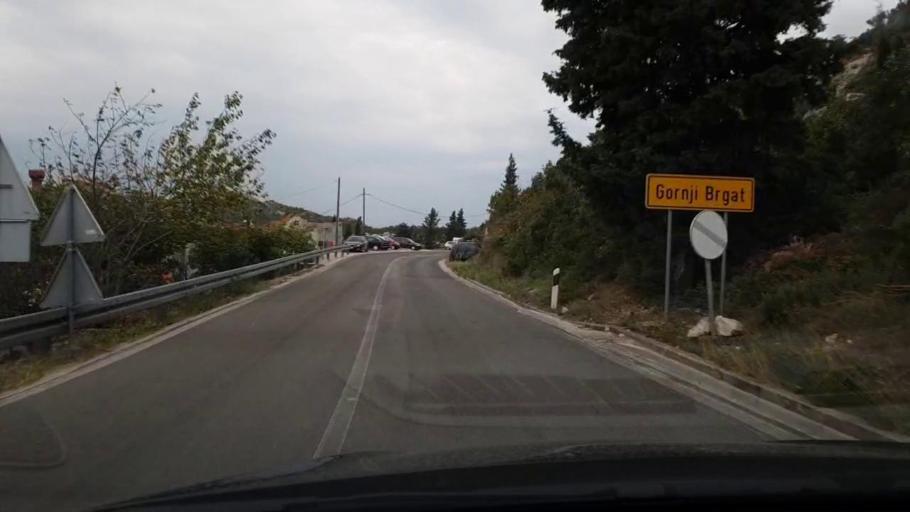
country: HR
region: Dubrovacko-Neretvanska
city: Cibaca
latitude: 42.6483
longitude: 18.1592
